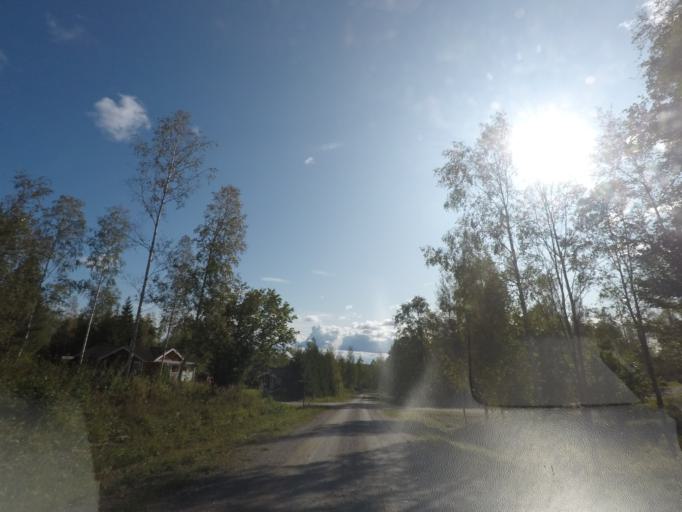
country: SE
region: Vaestmanland
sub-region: Skinnskattebergs Kommun
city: Skinnskatteberg
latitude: 59.8288
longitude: 15.5214
